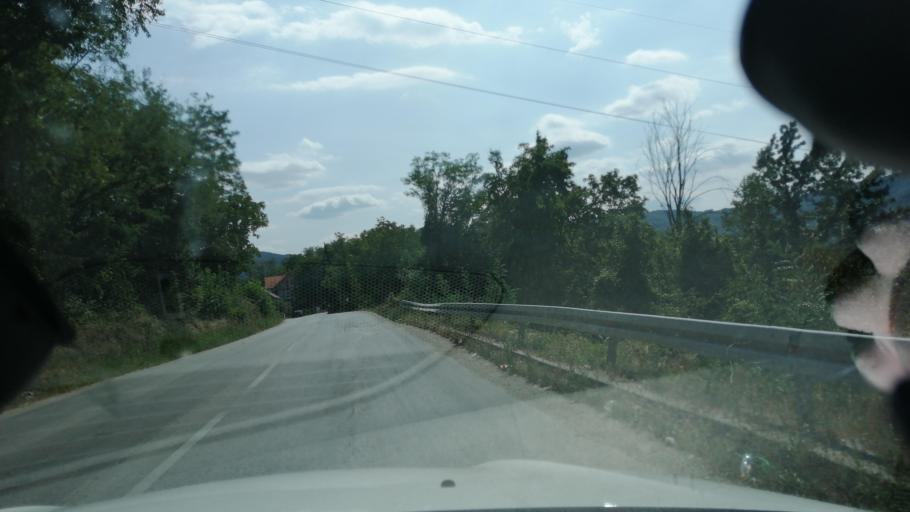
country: RS
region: Central Serbia
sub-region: Moravicki Okrug
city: Cacak
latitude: 43.8728
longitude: 20.3200
